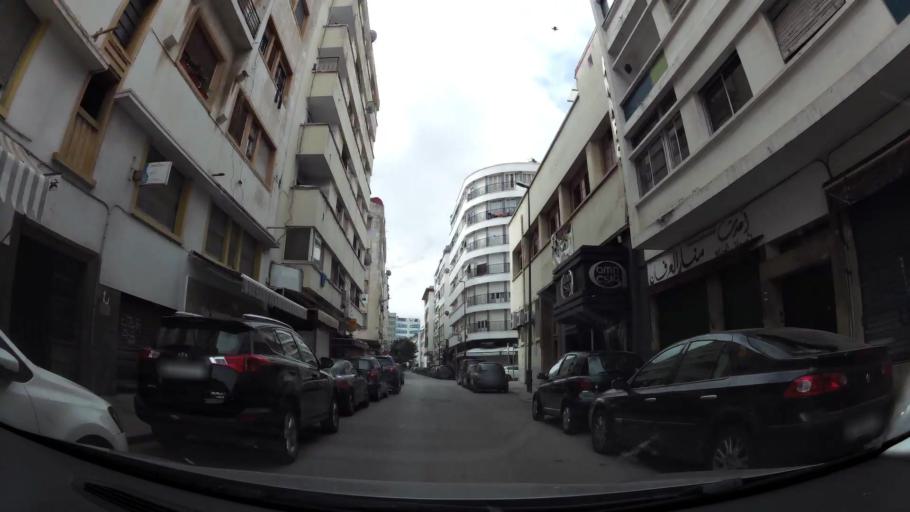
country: MA
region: Rabat-Sale-Zemmour-Zaer
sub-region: Rabat
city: Rabat
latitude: 34.0219
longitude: -6.8361
